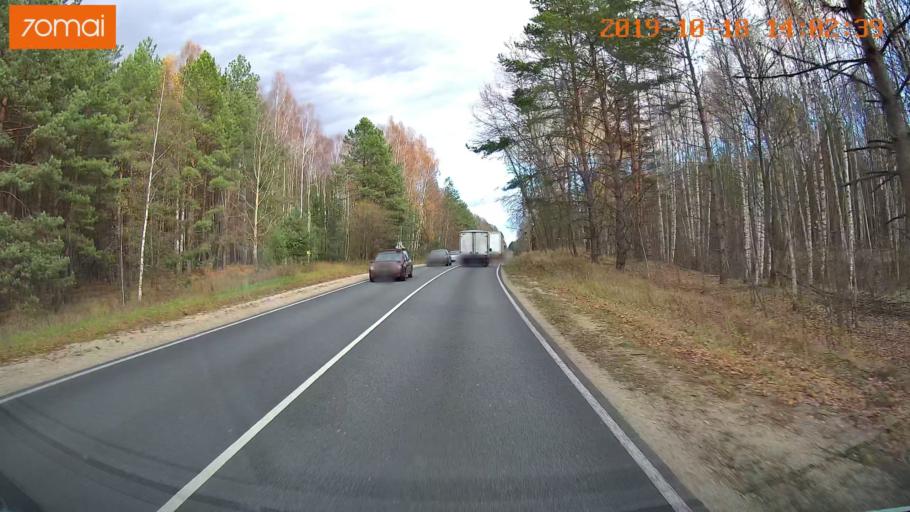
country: RU
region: Rjazan
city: Spas-Klepiki
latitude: 55.1142
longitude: 40.1115
